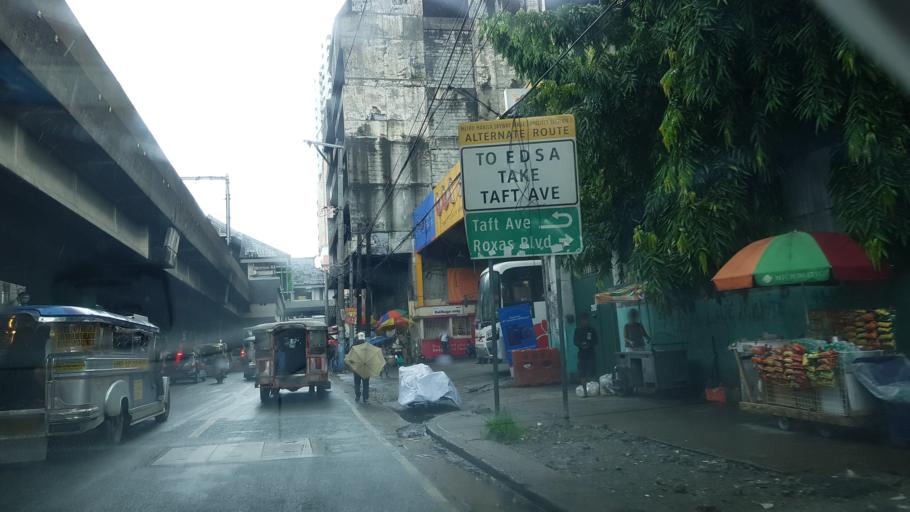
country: PH
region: Metro Manila
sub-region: Makati City
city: Makati City
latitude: 14.5555
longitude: 120.9967
